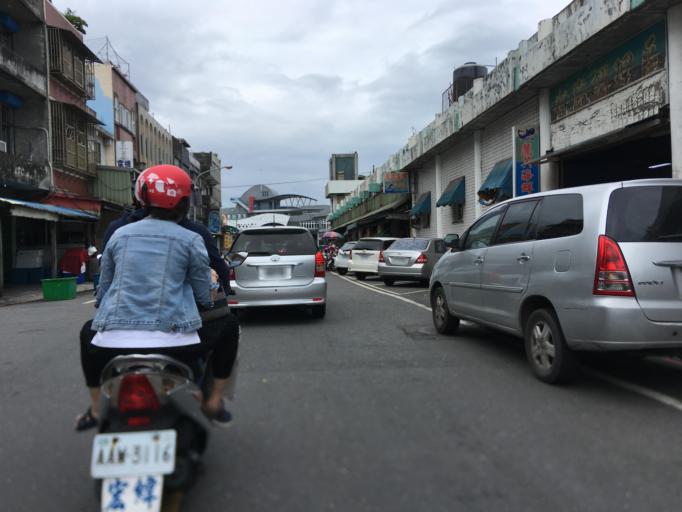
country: TW
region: Taiwan
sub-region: Yilan
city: Yilan
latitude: 24.5809
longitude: 121.8702
